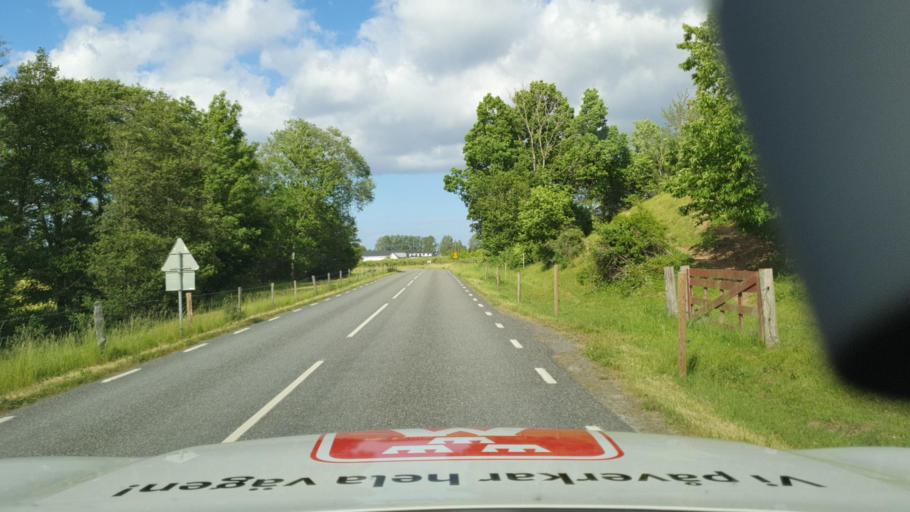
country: SE
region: Skane
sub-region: Simrishamns Kommun
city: Kivik
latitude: 55.6226
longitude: 14.2474
